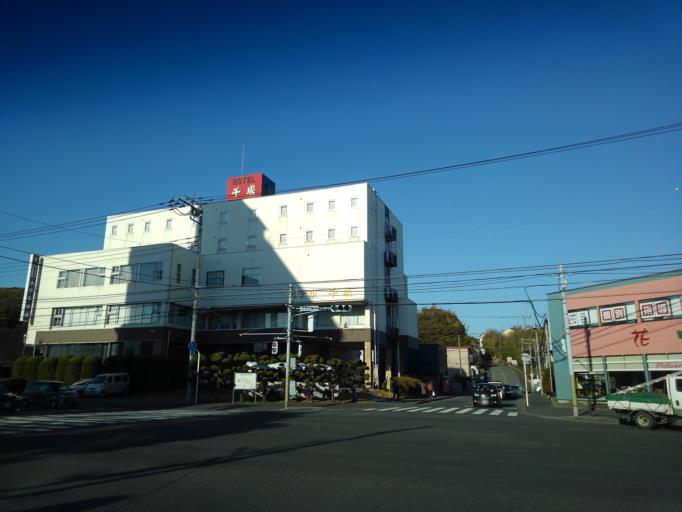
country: JP
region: Chiba
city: Kimitsu
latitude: 35.3359
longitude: 139.8952
